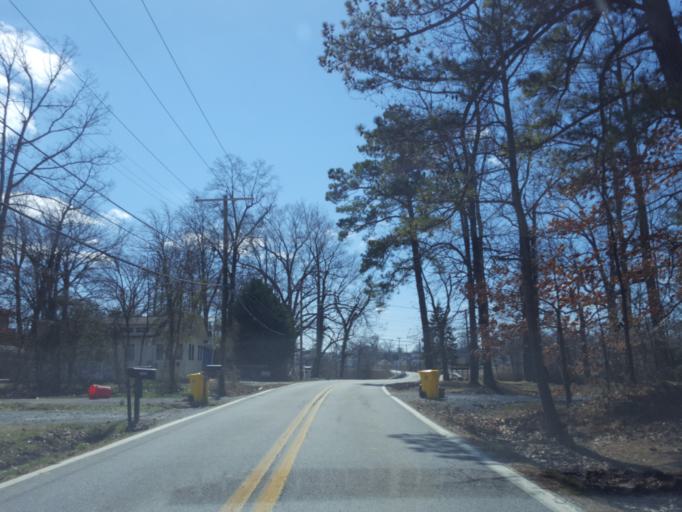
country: US
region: Maryland
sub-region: Calvert County
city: North Beach
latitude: 38.7147
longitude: -76.5293
